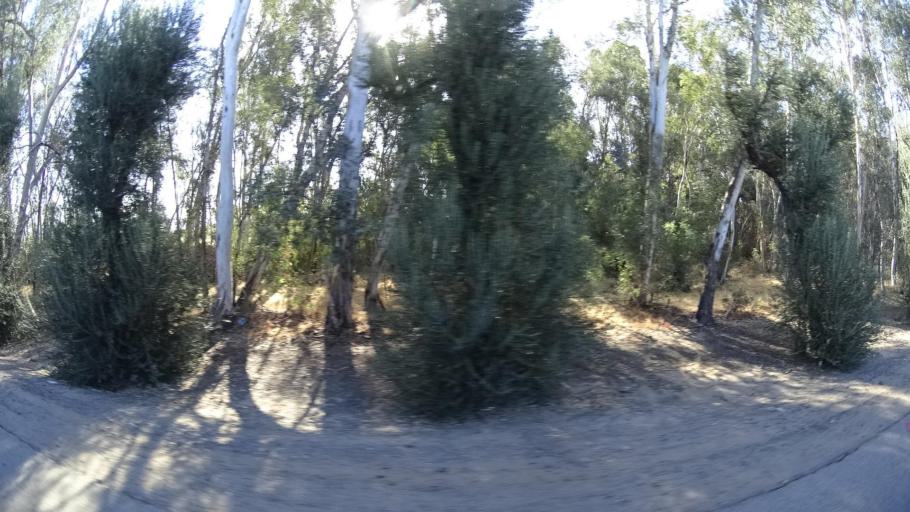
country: US
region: California
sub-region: Fresno County
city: Sunnyside
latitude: 36.7342
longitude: -119.6641
